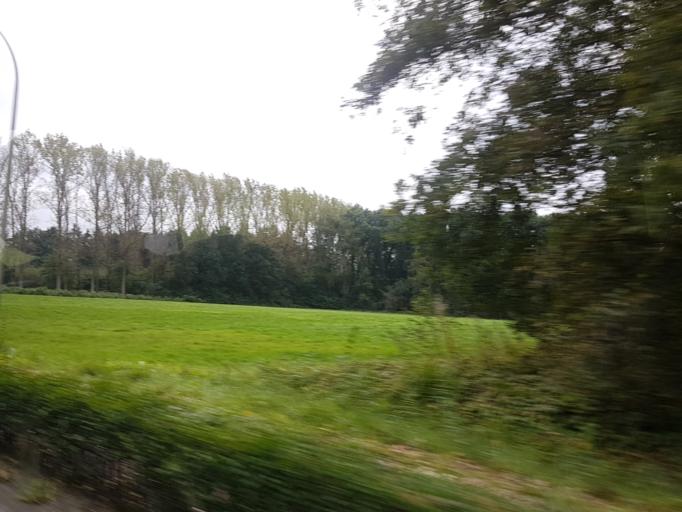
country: BE
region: Flanders
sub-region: Provincie Antwerpen
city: Zandhoven
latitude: 51.2081
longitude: 4.6299
